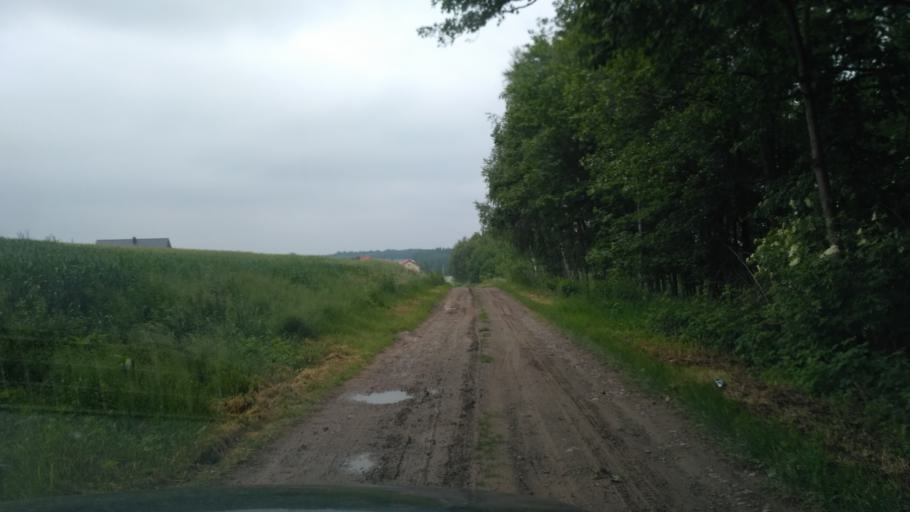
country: PL
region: Subcarpathian Voivodeship
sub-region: Powiat ropczycko-sedziszowski
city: Zagorzyce
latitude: 49.9853
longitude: 21.7058
